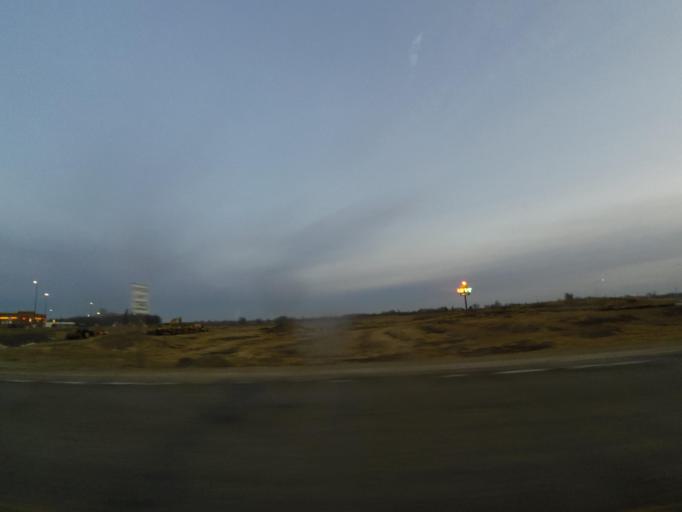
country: US
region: Iowa
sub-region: Floyd County
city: Charles City
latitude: 43.1222
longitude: -92.7374
